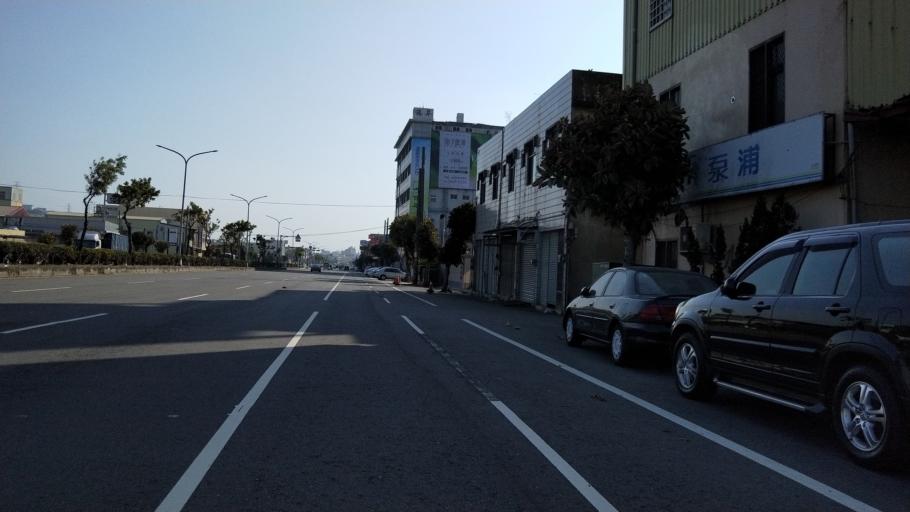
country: TW
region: Taiwan
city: Fengyuan
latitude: 24.2897
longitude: 120.5865
